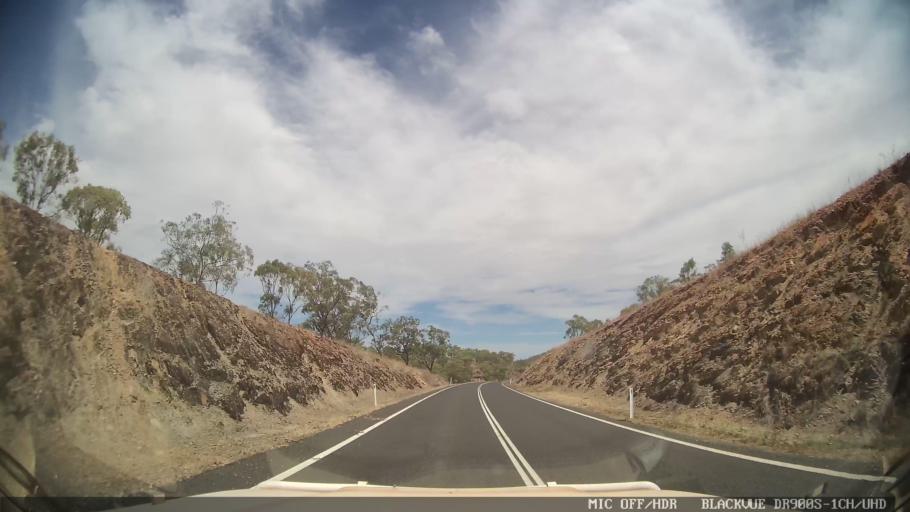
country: AU
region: Queensland
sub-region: Cairns
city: Port Douglas
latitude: -16.1494
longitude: 144.7663
